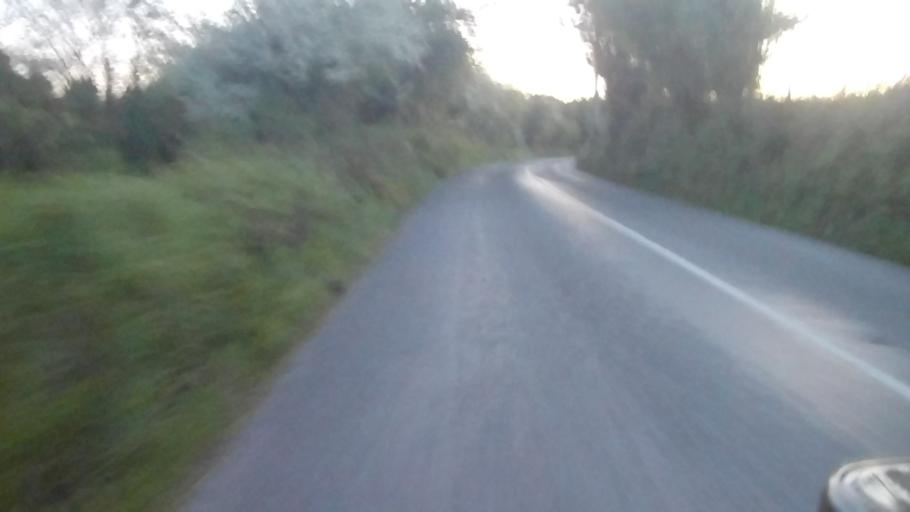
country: IE
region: Munster
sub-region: County Cork
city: Passage West
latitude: 51.9390
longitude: -8.3252
